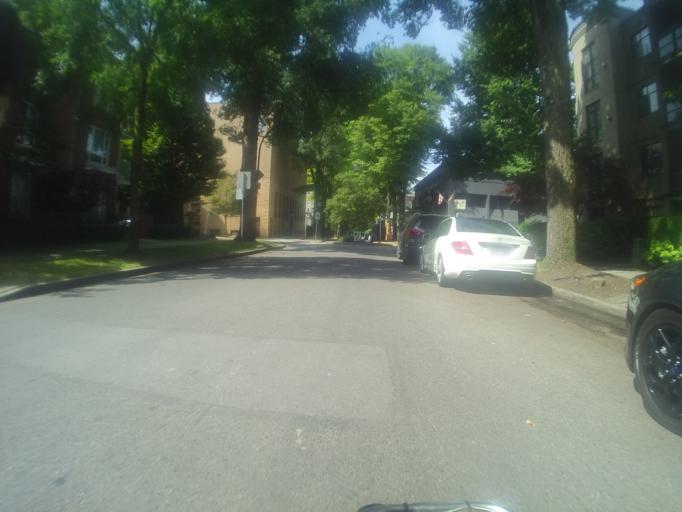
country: CA
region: British Columbia
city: West End
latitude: 49.2629
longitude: -123.1548
